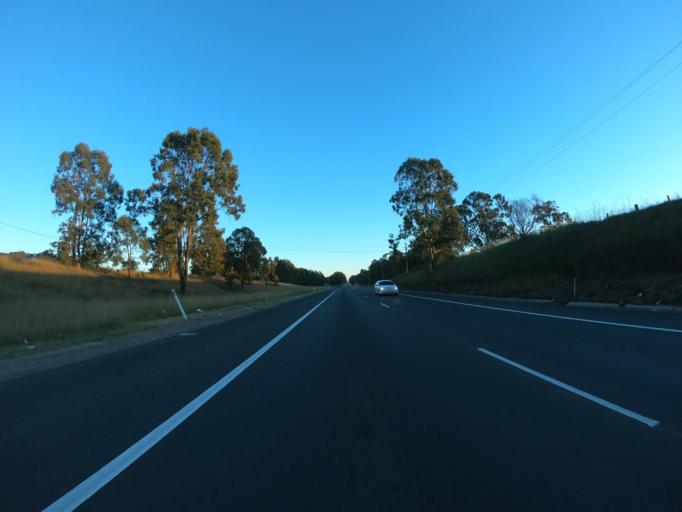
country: AU
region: New South Wales
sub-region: Hawkesbury
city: South Windsor
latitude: -33.6743
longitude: 150.8090
